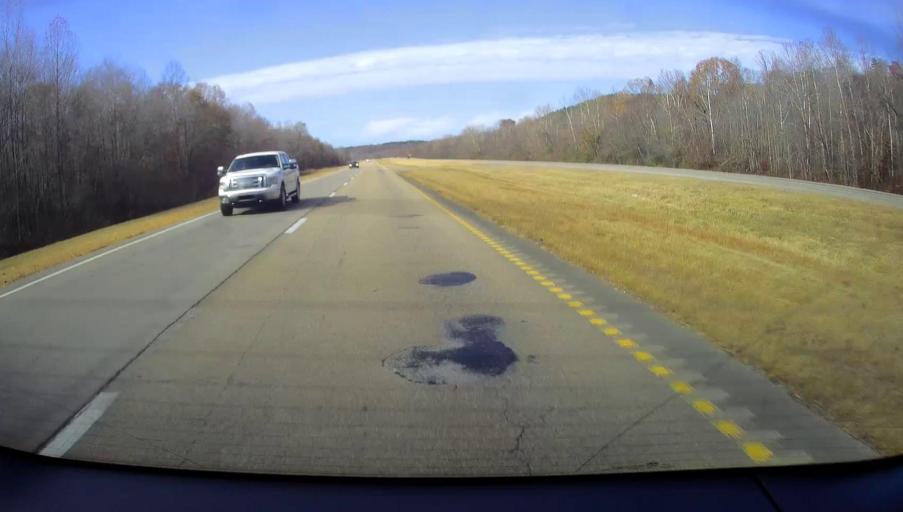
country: US
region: Mississippi
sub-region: Alcorn County
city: Corinth
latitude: 34.9389
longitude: -88.7785
